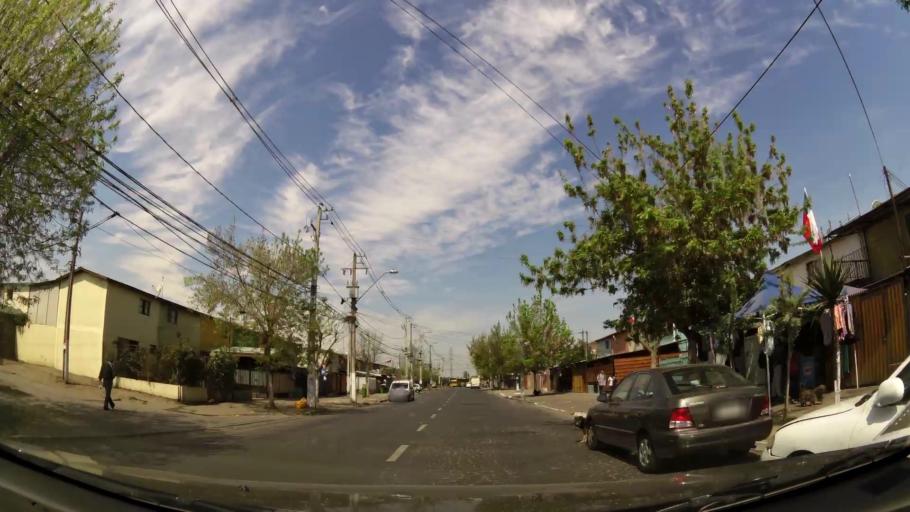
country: CL
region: Santiago Metropolitan
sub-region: Provincia de Cordillera
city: Puente Alto
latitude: -33.5901
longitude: -70.6009
